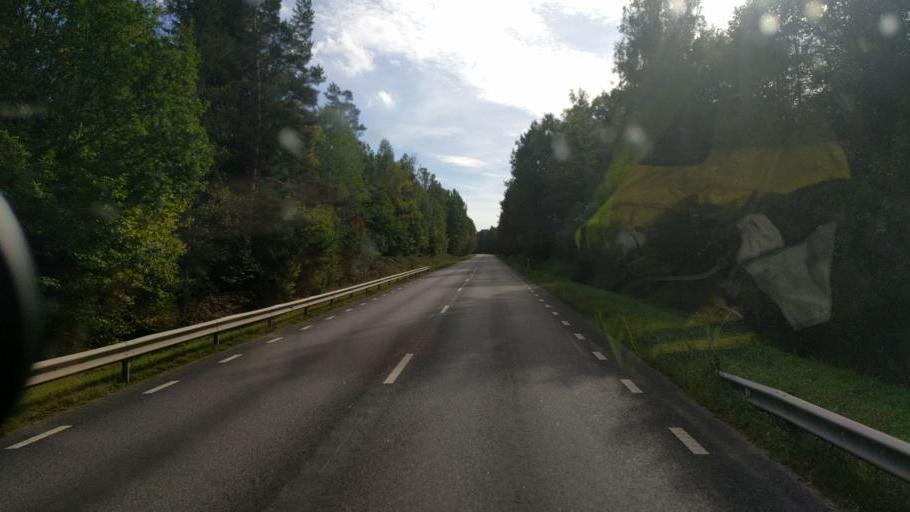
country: SE
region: OEstergoetland
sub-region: Kinda Kommun
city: Kisa
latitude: 57.9442
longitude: 15.6668
